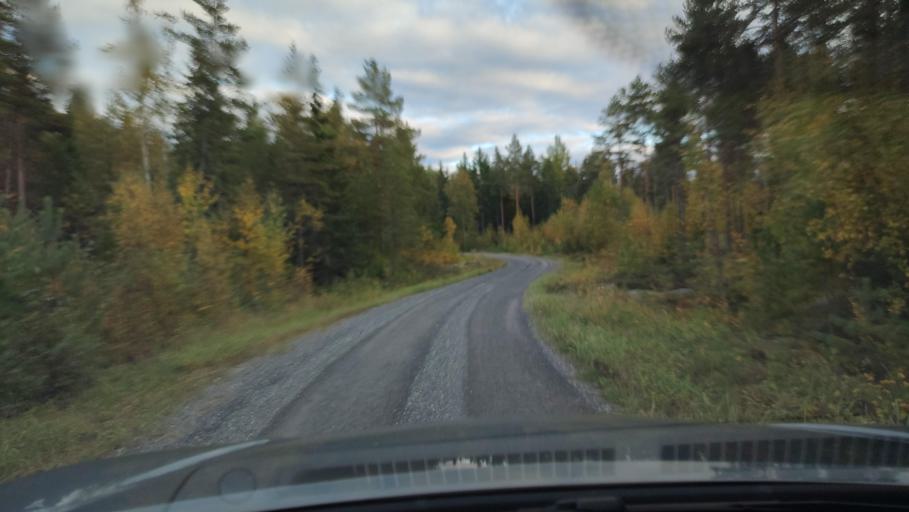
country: FI
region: Ostrobothnia
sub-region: Sydosterbotten
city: Kristinestad
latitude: 62.2311
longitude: 21.4183
